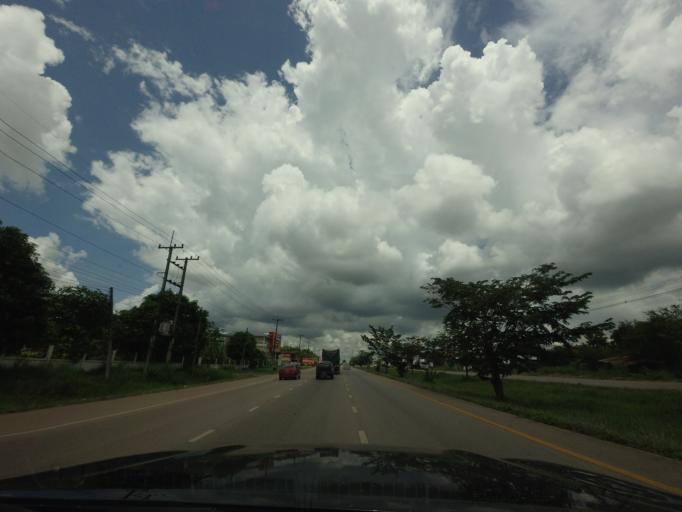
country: TH
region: Changwat Udon Thani
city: Udon Thani
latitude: 17.5296
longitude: 102.7996
